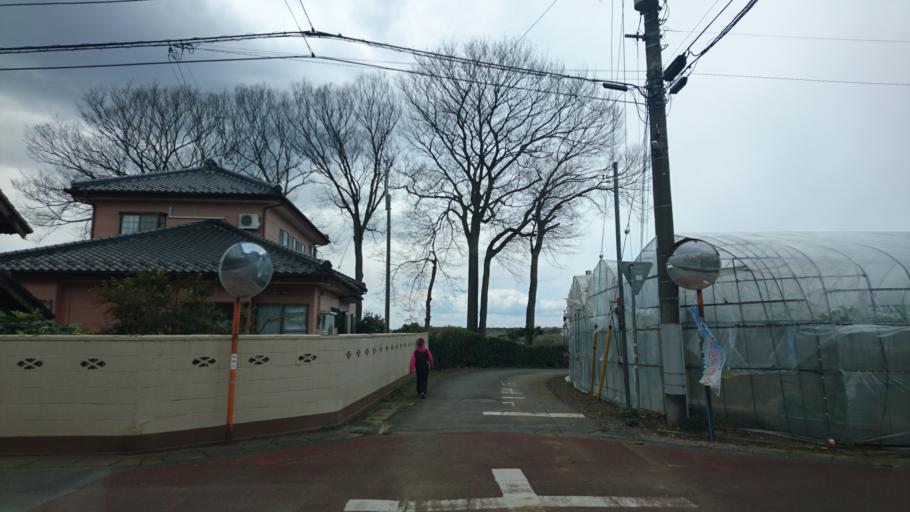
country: JP
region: Ibaraki
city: Yuki
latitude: 36.2864
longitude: 139.9125
